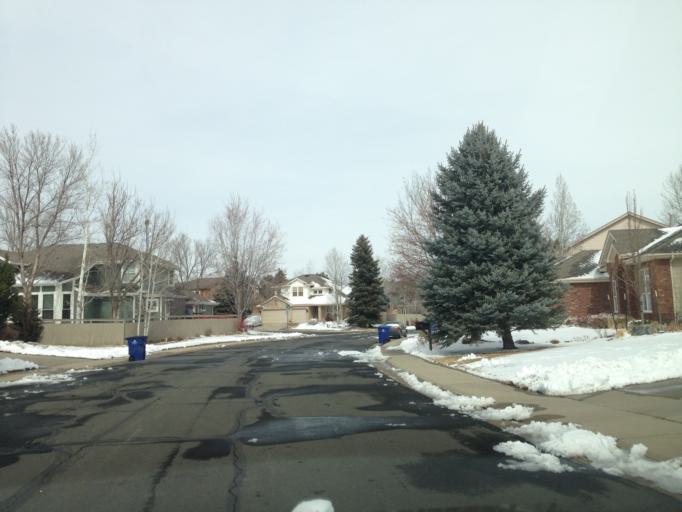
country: US
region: Colorado
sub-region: Boulder County
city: Lafayette
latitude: 39.9708
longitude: -105.0993
